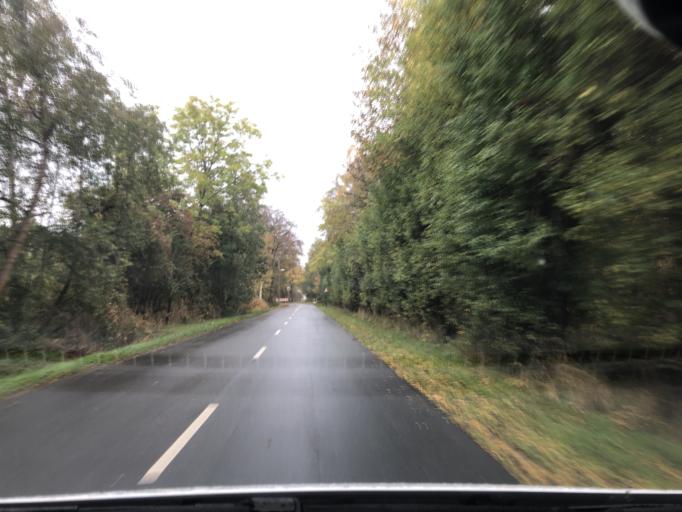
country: DK
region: Capital Region
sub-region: Tarnby Kommune
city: Tarnby
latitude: 55.5641
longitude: 12.5866
